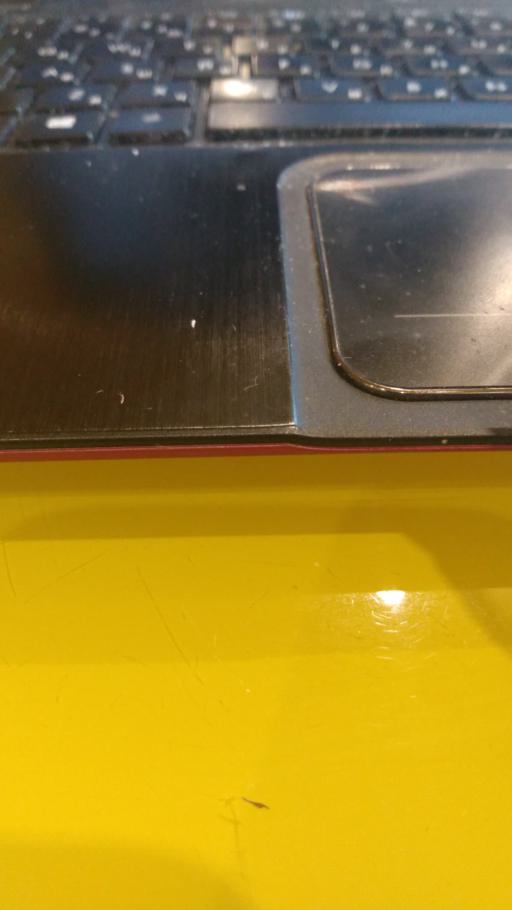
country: RU
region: Tverskaya
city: Vydropuzhsk
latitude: 57.2507
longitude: 34.9452
